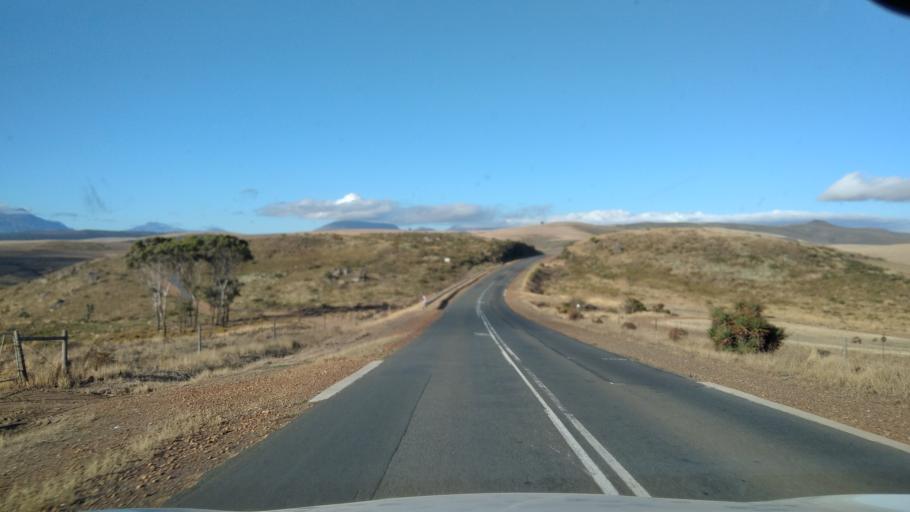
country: ZA
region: Western Cape
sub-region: Overberg District Municipality
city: Caledon
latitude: -34.1786
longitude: 19.2782
